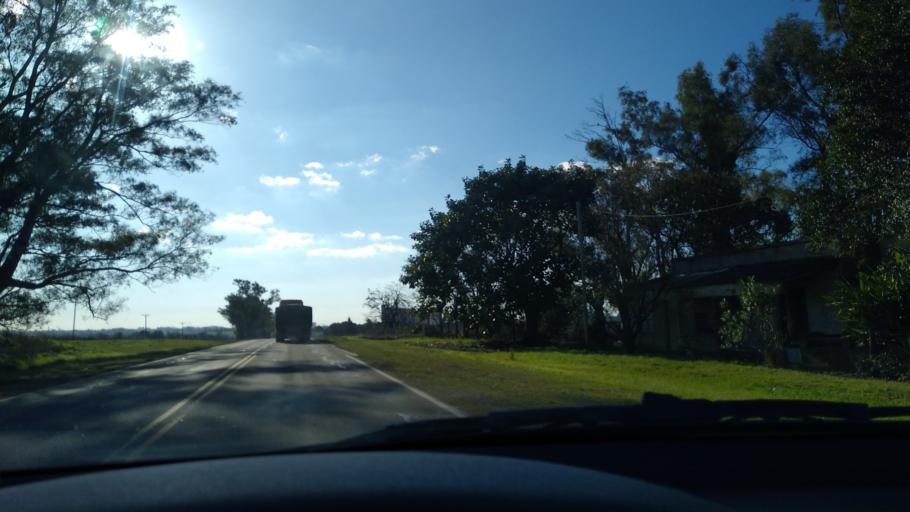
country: AR
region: Entre Rios
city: Diamante
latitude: -32.0972
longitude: -60.5892
